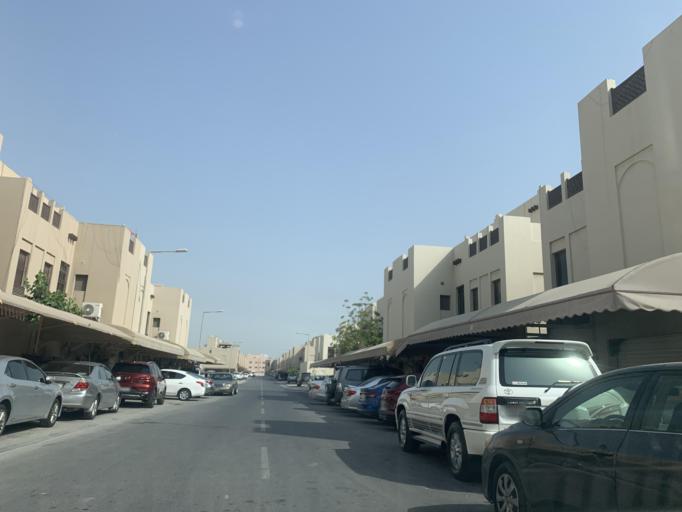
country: BH
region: Northern
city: Madinat `Isa
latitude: 26.1847
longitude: 50.5615
